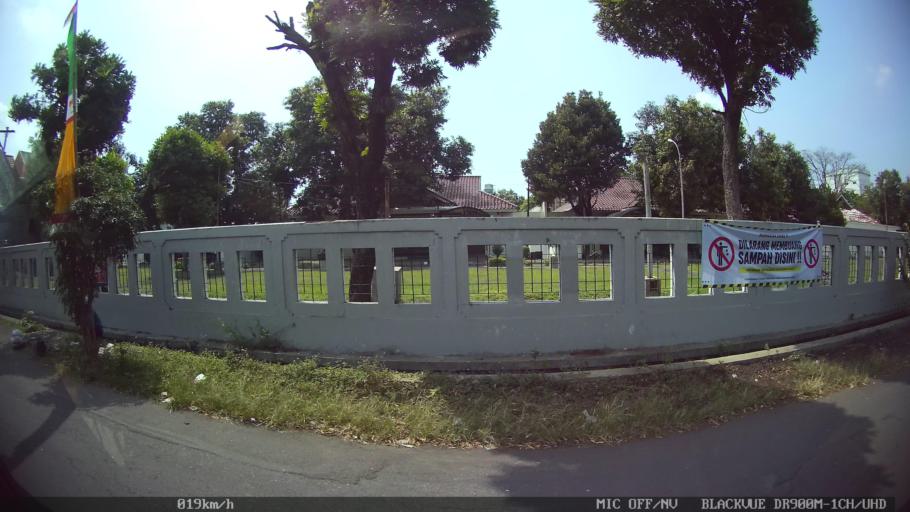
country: ID
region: Daerah Istimewa Yogyakarta
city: Yogyakarta
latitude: -7.7995
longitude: 110.3941
